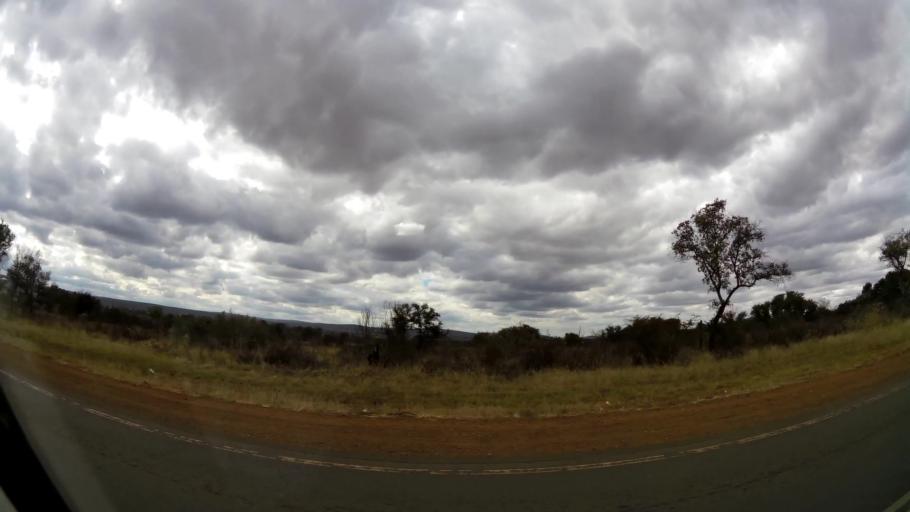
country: ZA
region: Limpopo
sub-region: Waterberg District Municipality
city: Modimolle
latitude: -24.7235
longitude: 28.4255
